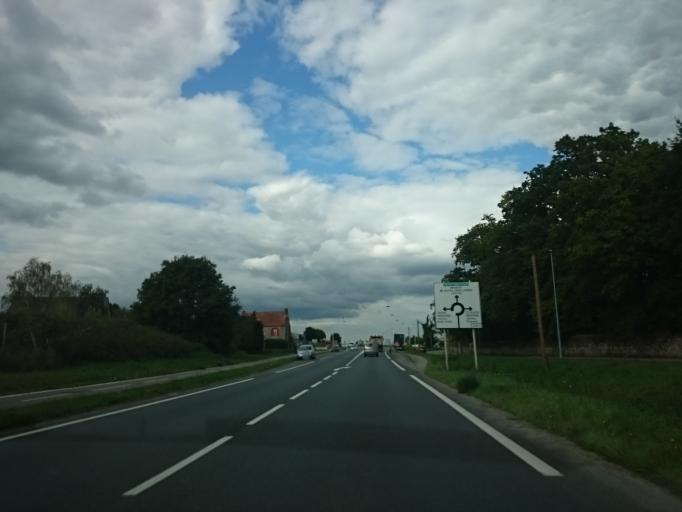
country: FR
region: Pays de la Loire
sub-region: Departement de la Loire-Atlantique
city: Saint-Herblain
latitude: 47.2250
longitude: -1.6526
